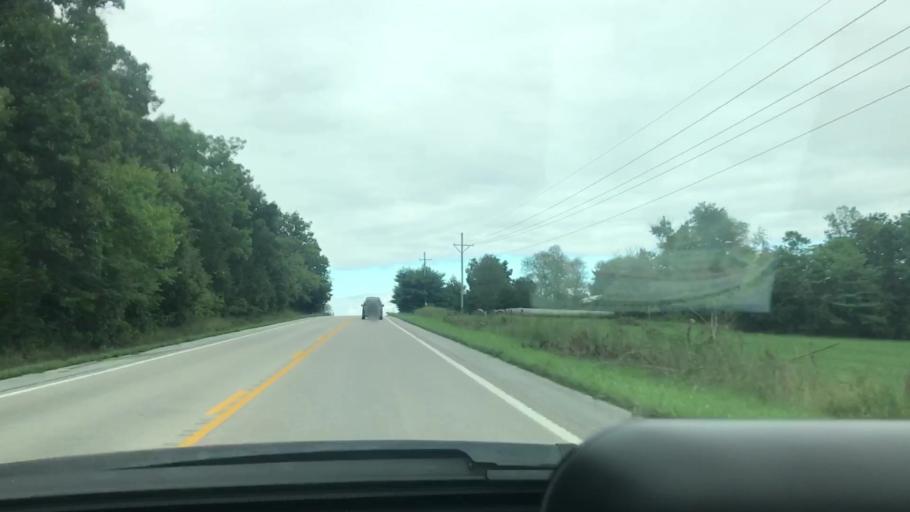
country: US
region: Missouri
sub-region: Hickory County
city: Hermitage
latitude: 37.8776
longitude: -93.1804
